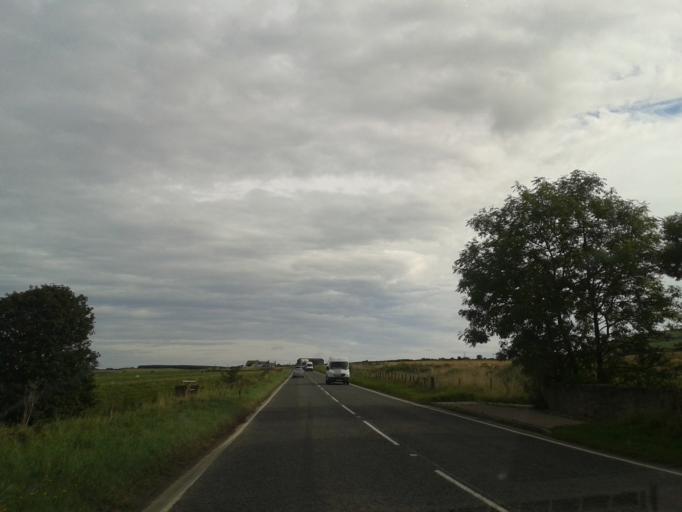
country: GB
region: Scotland
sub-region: Moray
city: Cullen
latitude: 57.6781
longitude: -2.7580
